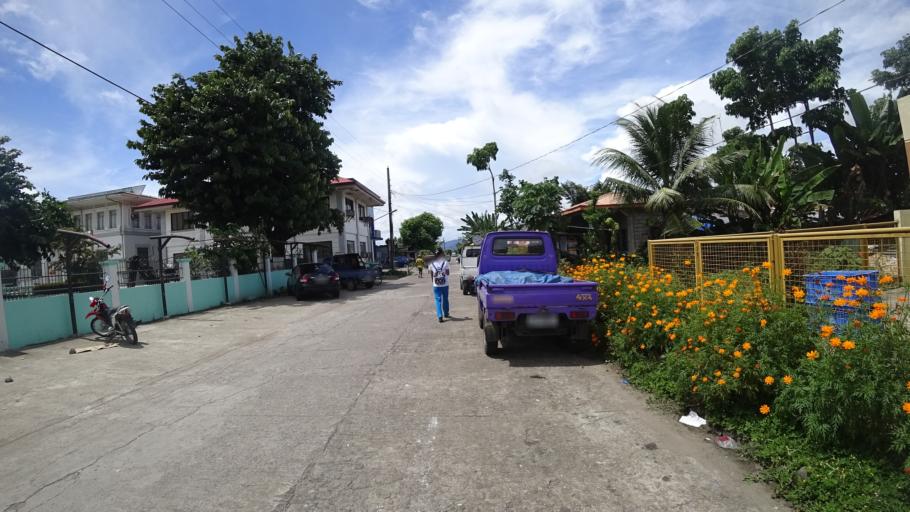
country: PH
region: Eastern Visayas
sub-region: Province of Leyte
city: Alangalang
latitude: 11.2068
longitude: 124.8471
